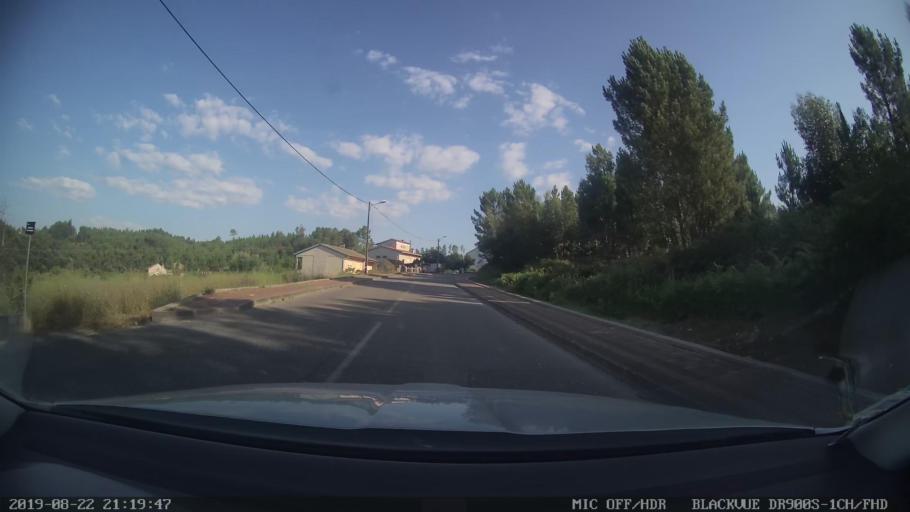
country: PT
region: Castelo Branco
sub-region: Serta
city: Serta
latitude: 39.8084
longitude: -8.1082
